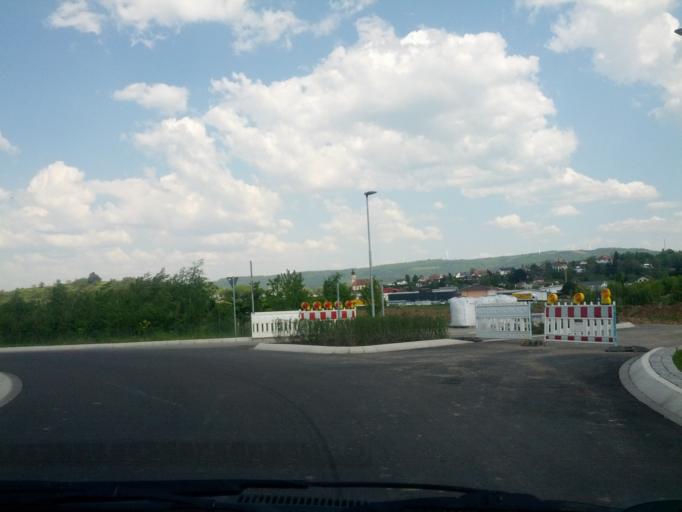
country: DE
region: Baden-Wuerttemberg
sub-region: Freiburg Region
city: Ettenheim
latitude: 48.2634
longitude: 7.8012
